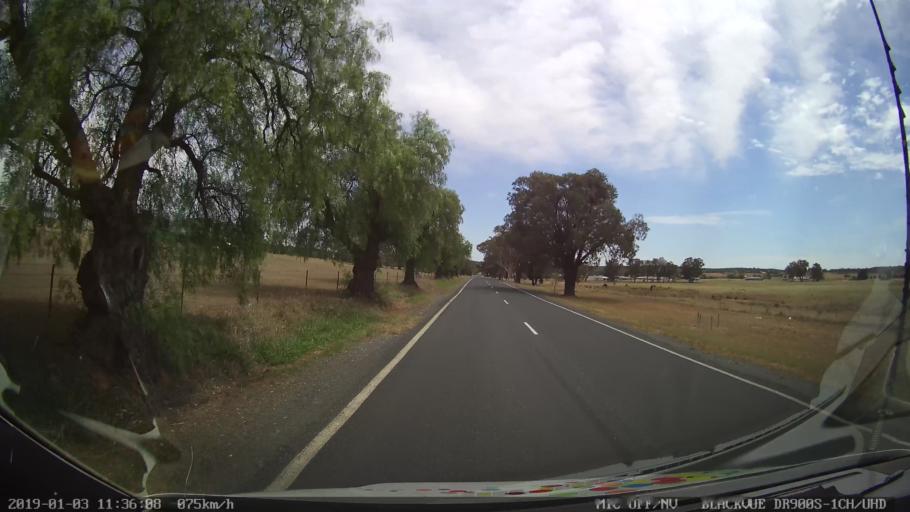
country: AU
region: New South Wales
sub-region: Weddin
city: Grenfell
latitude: -33.9142
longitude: 148.1595
